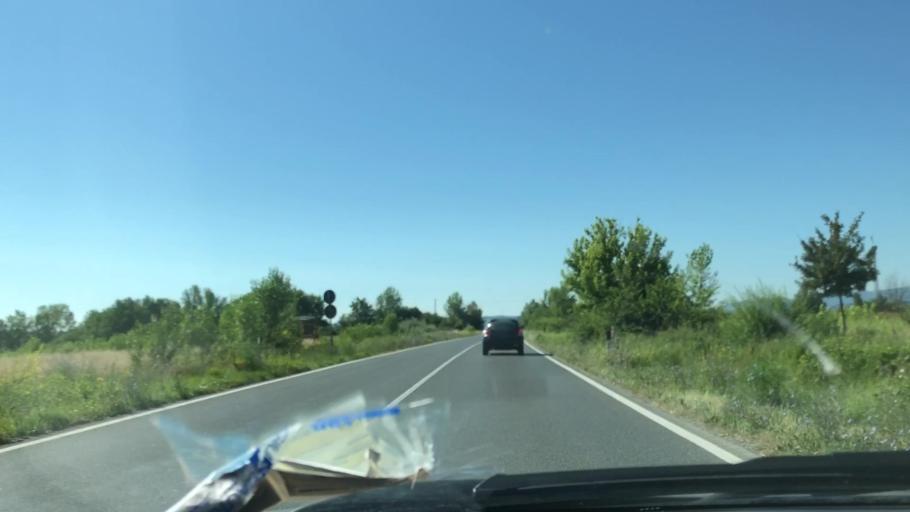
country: IT
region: Tuscany
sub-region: Province of Pisa
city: Forcoli
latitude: 43.5988
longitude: 10.6959
